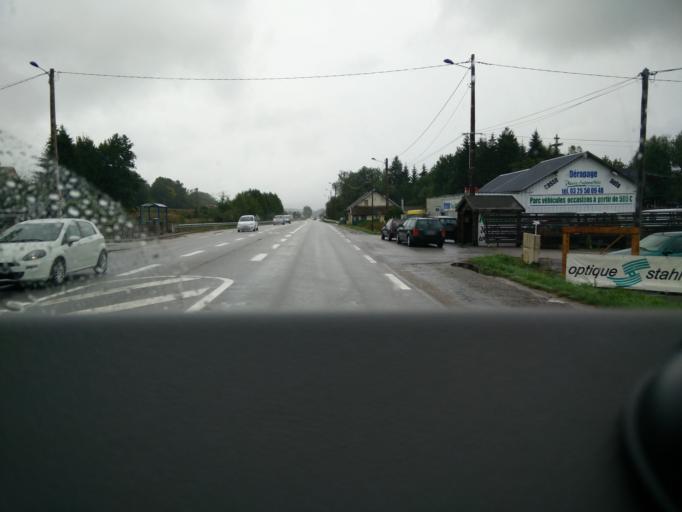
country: FR
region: Lorraine
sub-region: Departement des Vosges
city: Saint-Leonard
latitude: 48.2294
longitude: 6.9486
